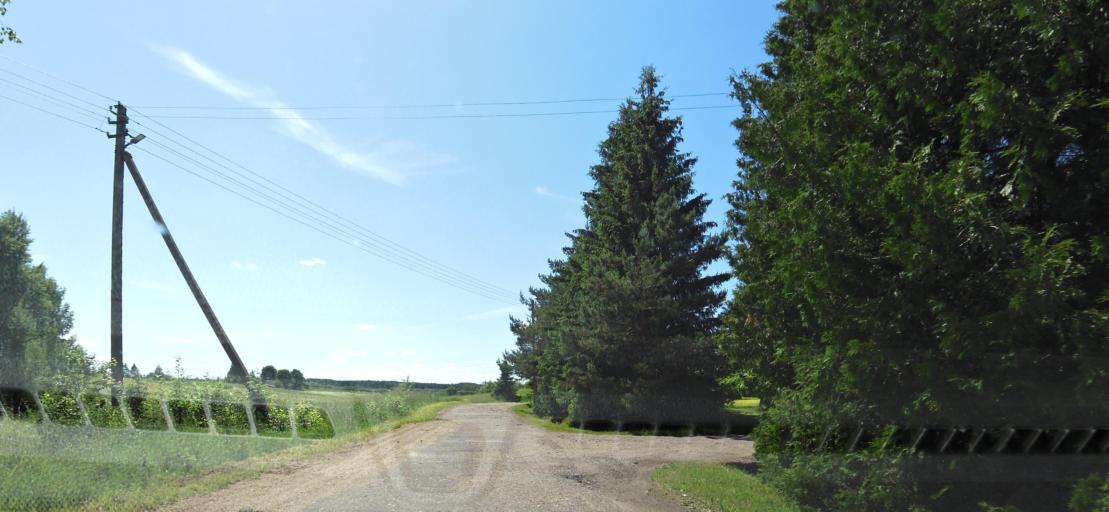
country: LT
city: Sirvintos
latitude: 55.2140
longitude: 25.1064
